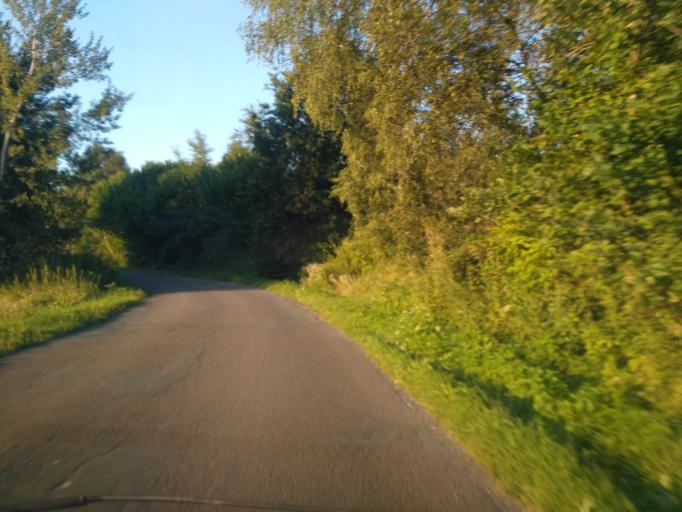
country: PL
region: Subcarpathian Voivodeship
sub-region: Powiat strzyzowski
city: Wysoka Strzyzowska
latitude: 49.8049
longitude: 21.7471
